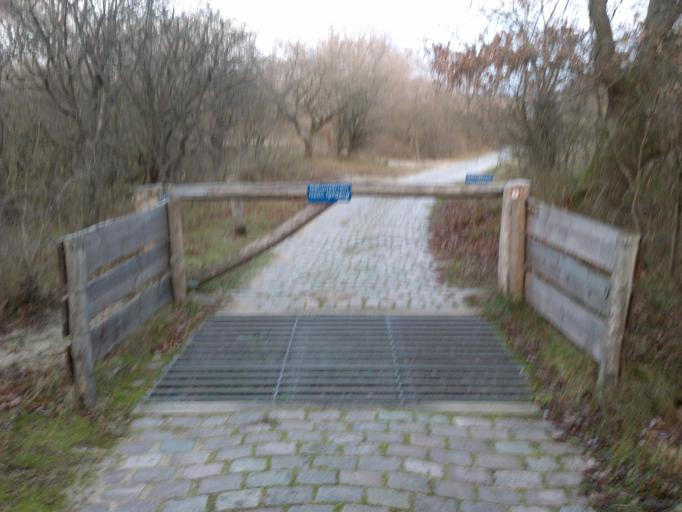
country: NL
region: South Holland
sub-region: Gemeente Wassenaar
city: Wassenaar
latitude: 52.1326
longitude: 4.3460
